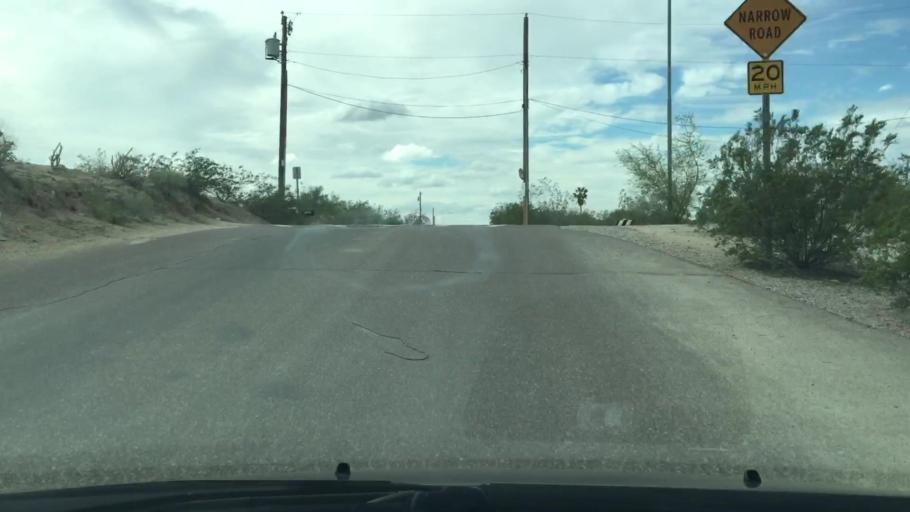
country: US
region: Arizona
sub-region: Maricopa County
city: Guadalupe
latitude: 33.3669
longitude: -112.0334
